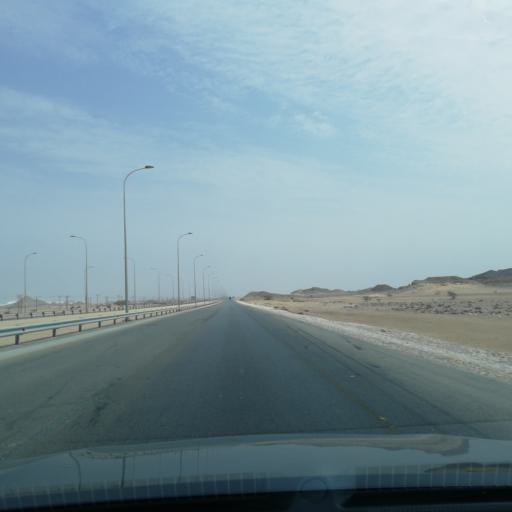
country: OM
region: Zufar
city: Salalah
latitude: 17.4528
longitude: 54.0477
